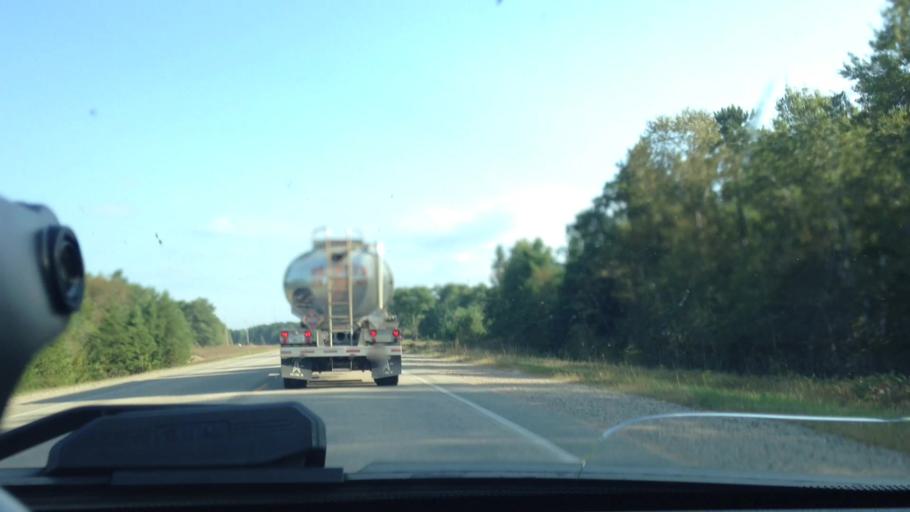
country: US
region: Wisconsin
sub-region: Marinette County
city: Niagara
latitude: 45.6556
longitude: -87.9624
